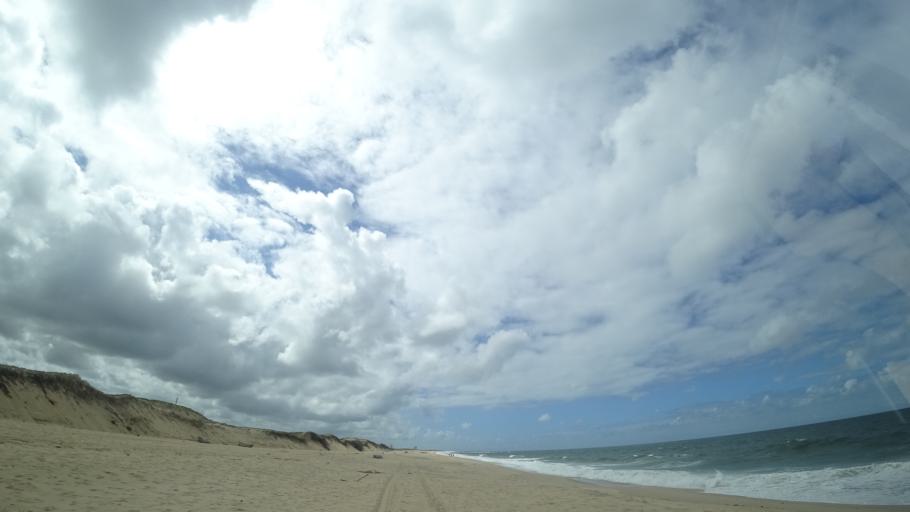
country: MZ
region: Sofala
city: Beira
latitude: -19.6150
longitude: 35.2213
